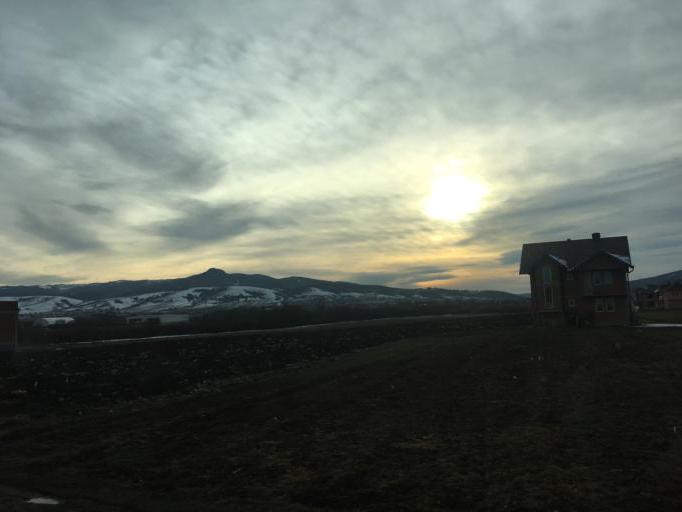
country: XK
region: Pristina
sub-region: Komuna e Drenasit
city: Glogovac
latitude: 42.5850
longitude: 20.8982
